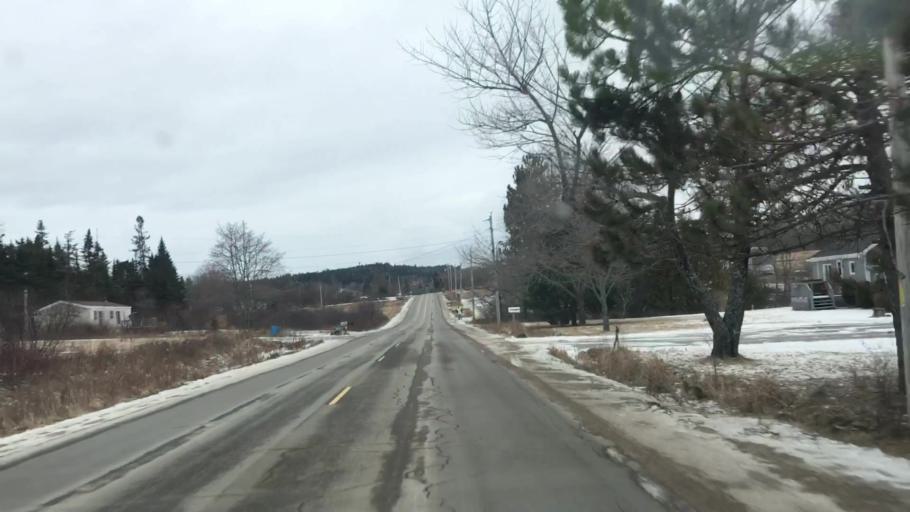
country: US
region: Maine
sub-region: Washington County
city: Machiasport
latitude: 44.7091
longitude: -67.4027
